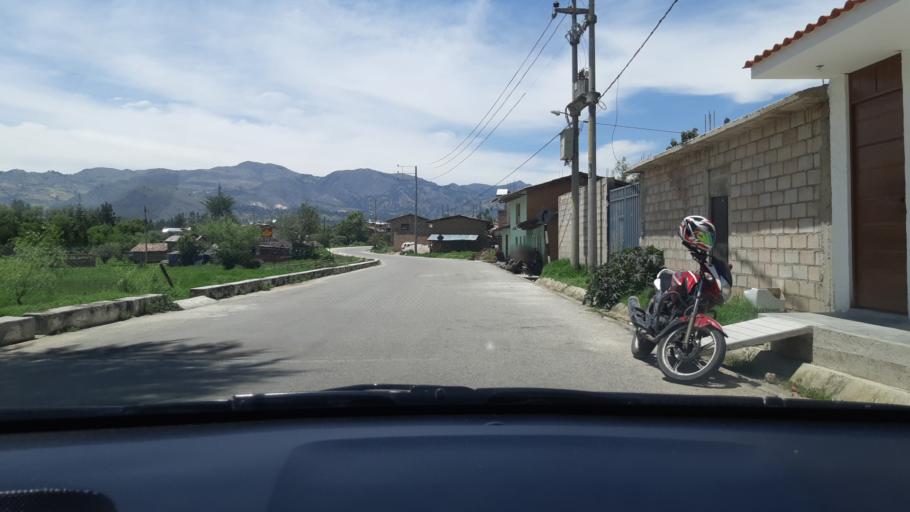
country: PE
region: Cajamarca
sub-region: Provincia de Cajamarca
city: Llacanora
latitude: -7.1829
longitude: -78.4461
